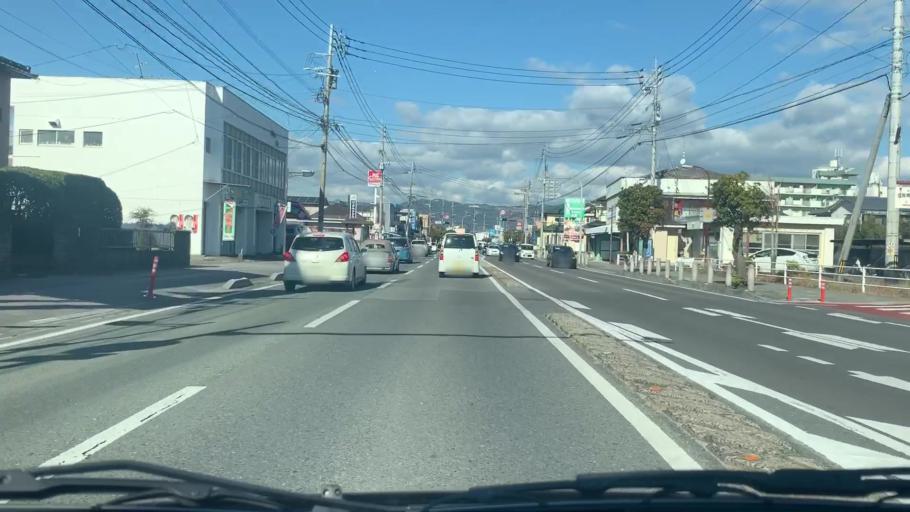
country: JP
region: Saga Prefecture
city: Saga-shi
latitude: 33.2784
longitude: 130.2927
